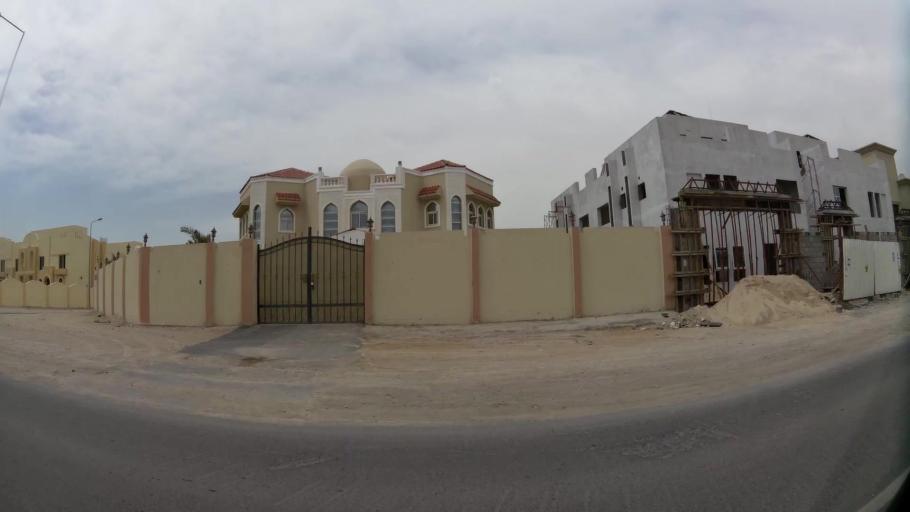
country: QA
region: Baladiyat ar Rayyan
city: Ar Rayyan
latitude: 25.2243
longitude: 51.4602
